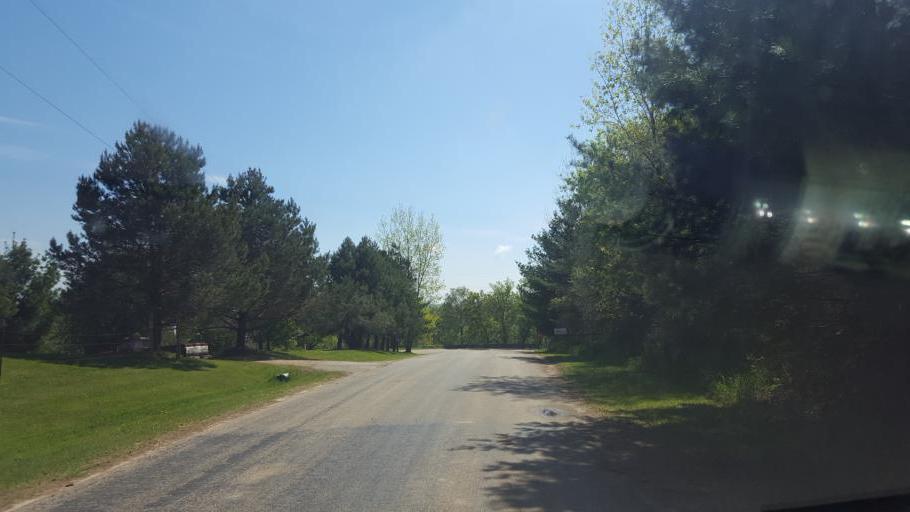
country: US
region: Wisconsin
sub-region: Juneau County
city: Elroy
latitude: 43.6952
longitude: -90.2922
